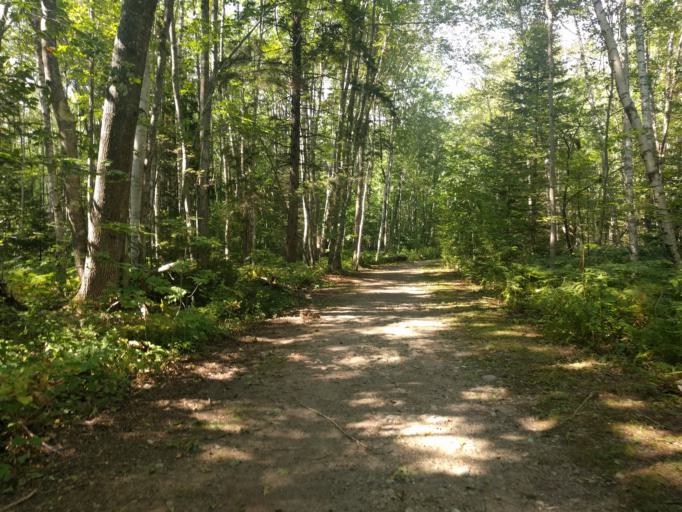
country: US
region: Maine
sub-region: Waldo County
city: Belfast
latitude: 44.4304
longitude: -68.9461
